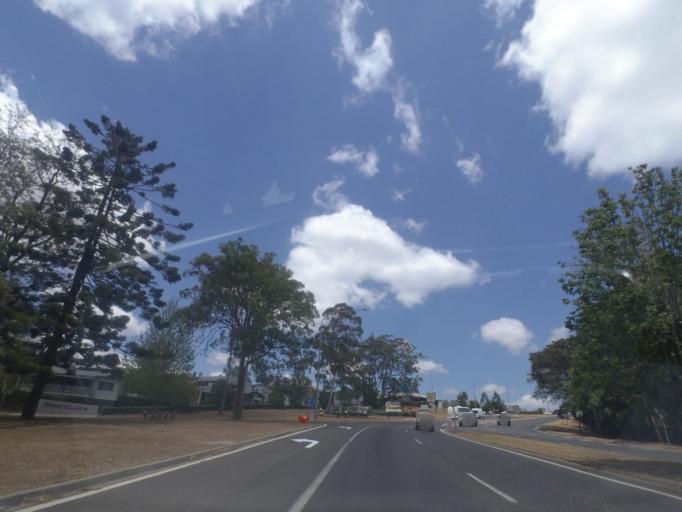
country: AU
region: Queensland
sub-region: Toowoomba
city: East Toowoomba
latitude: -27.5654
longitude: 151.9778
